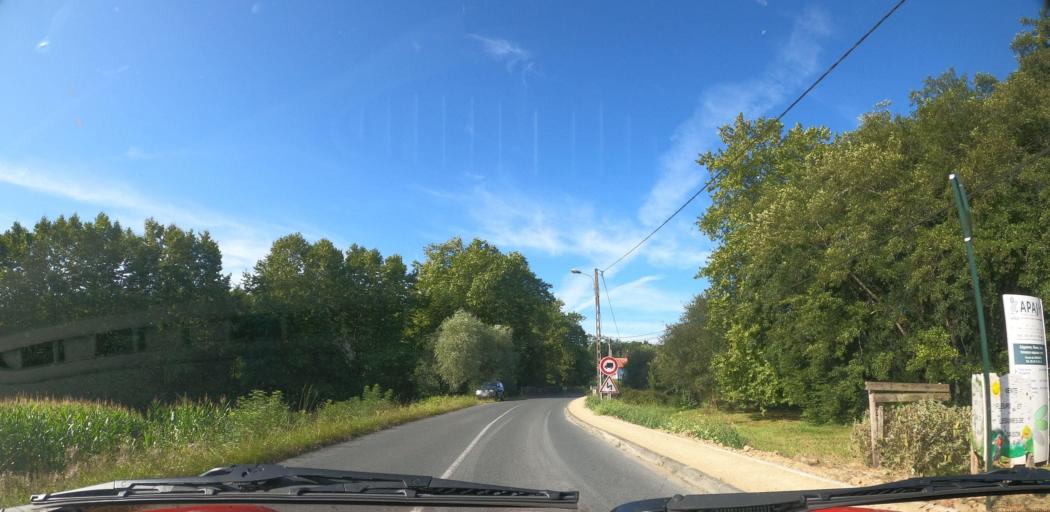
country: FR
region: Aquitaine
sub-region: Departement des Pyrenees-Atlantiques
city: Arbonne
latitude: 43.4369
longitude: -1.5512
